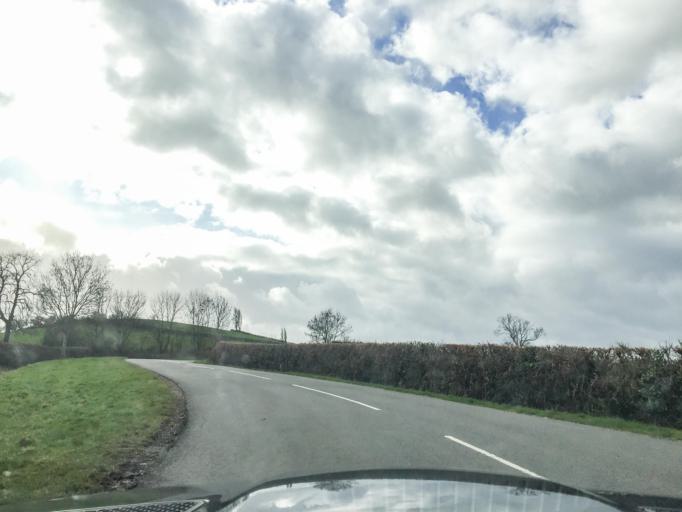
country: GB
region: England
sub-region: Warwickshire
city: Shipston on Stour
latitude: 52.0623
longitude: -1.5476
